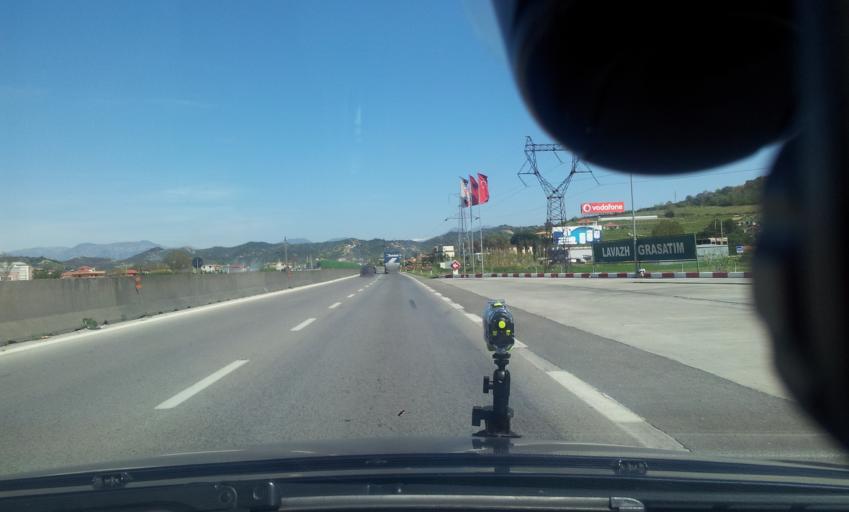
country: AL
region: Durres
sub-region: Rrethi i Durresit
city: Maminas
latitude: 41.3704
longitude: 19.5979
